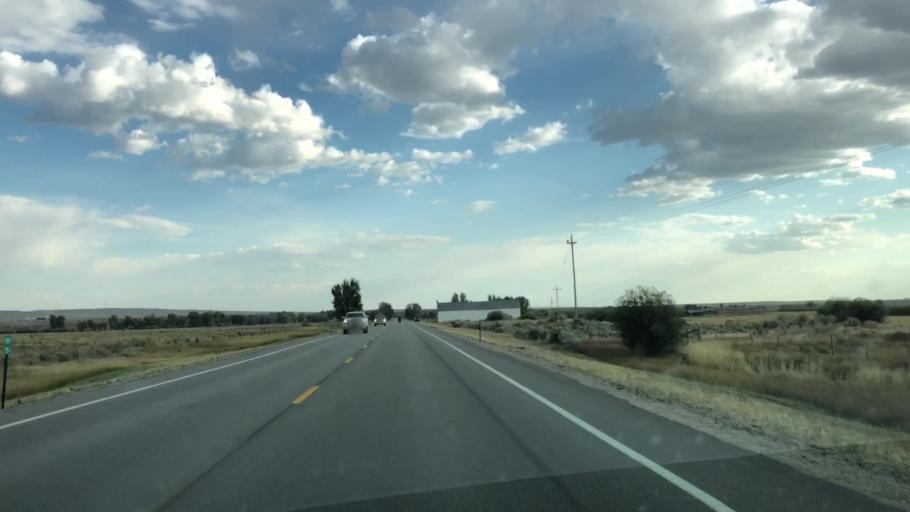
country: US
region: Wyoming
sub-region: Sublette County
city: Pinedale
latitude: 42.7069
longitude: -109.7141
